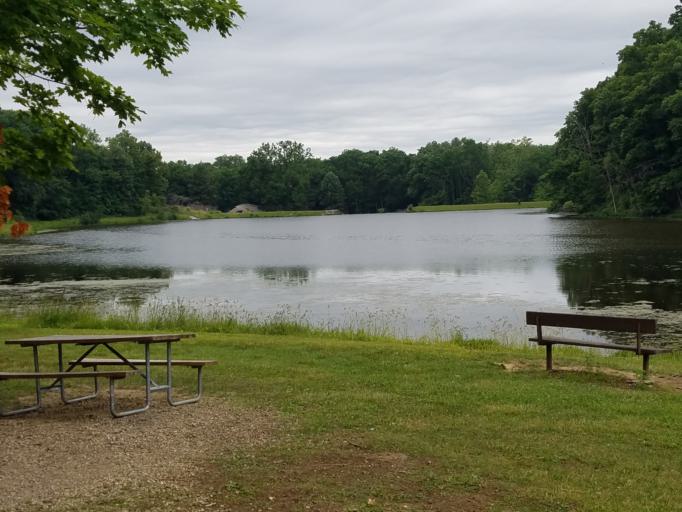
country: US
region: Ohio
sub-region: Morrow County
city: Mount Gilead
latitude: 40.5489
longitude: -82.8140
